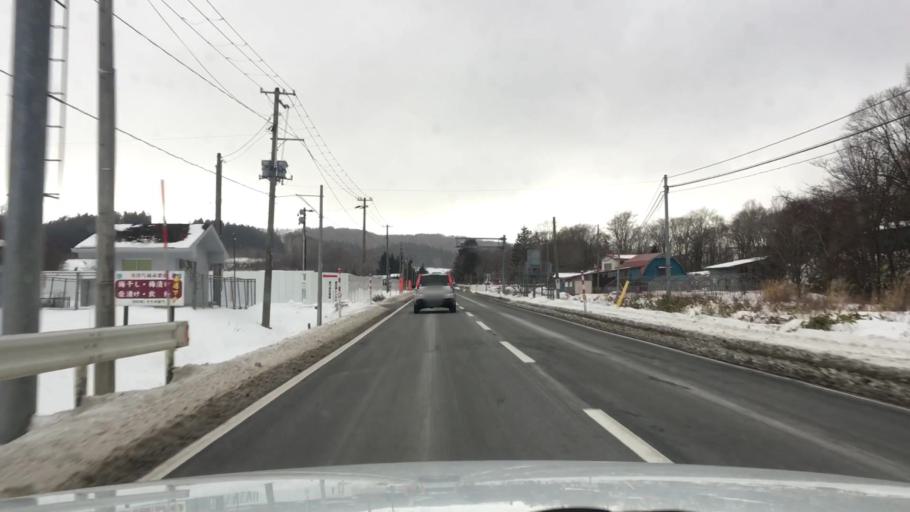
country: JP
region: Iwate
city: Morioka-shi
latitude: 39.6458
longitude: 141.3658
